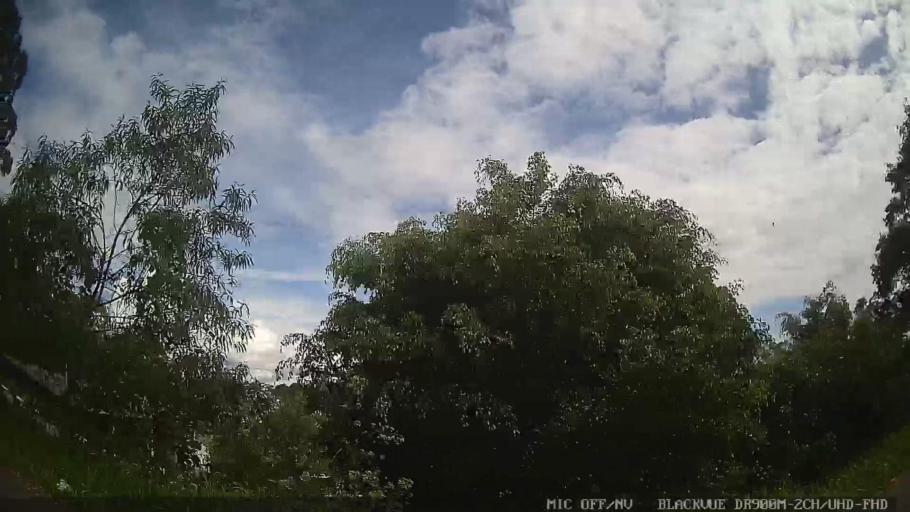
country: BR
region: Sao Paulo
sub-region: Mogi das Cruzes
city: Mogi das Cruzes
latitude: -23.5591
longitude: -46.1852
